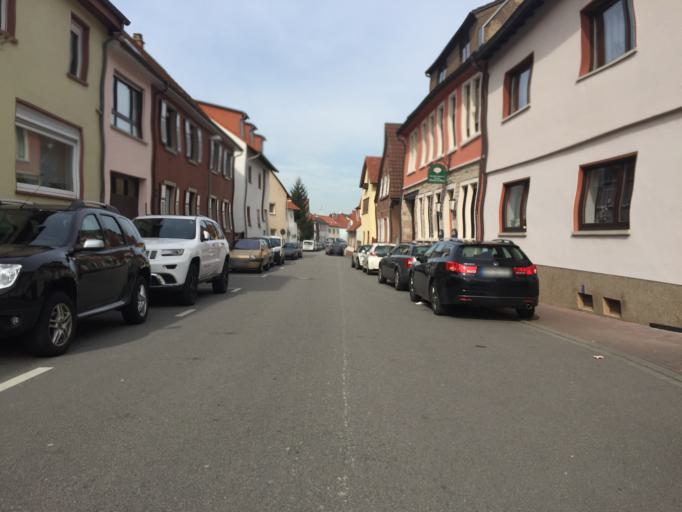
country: DE
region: Hesse
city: Viernheim
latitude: 49.5389
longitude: 8.5845
